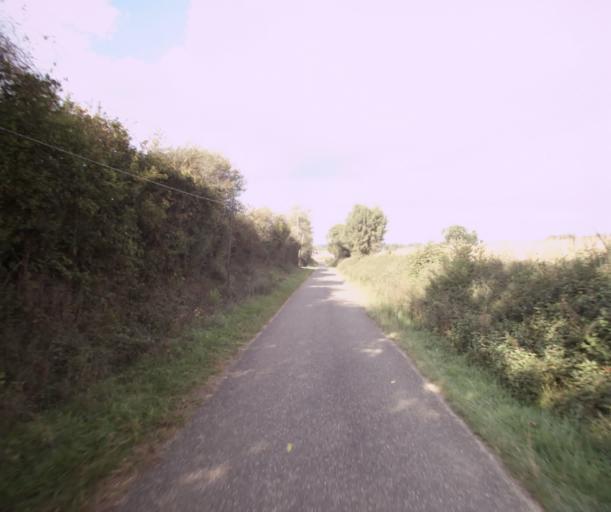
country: FR
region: Midi-Pyrenees
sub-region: Departement du Gers
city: Cazaubon
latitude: 43.8795
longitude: -0.0433
